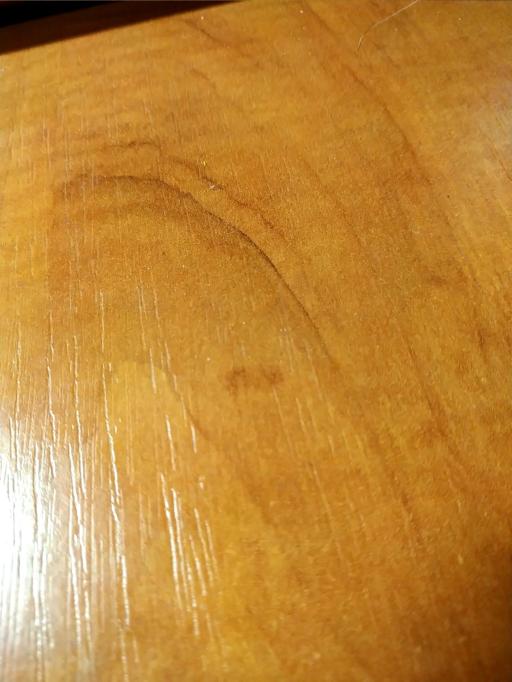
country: RU
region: Smolensk
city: Yartsevo
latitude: 55.4192
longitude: 32.8315
